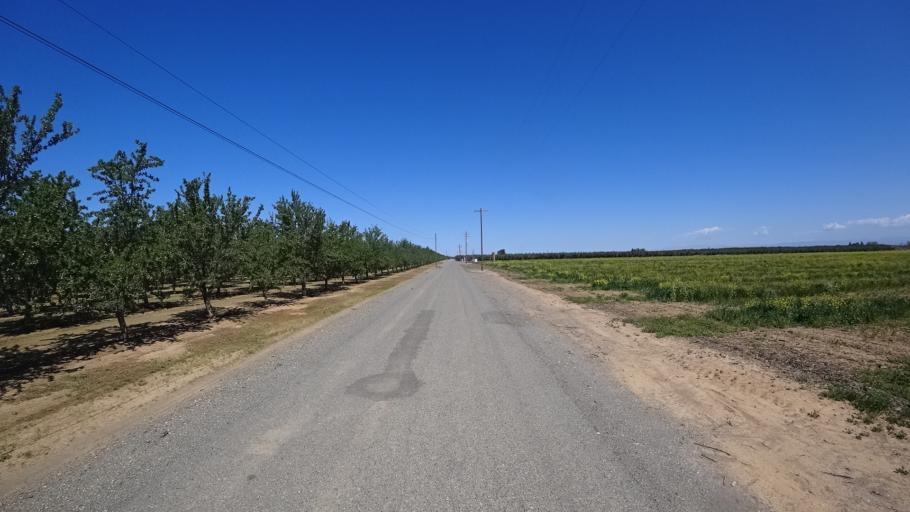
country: US
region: California
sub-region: Glenn County
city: Orland
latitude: 39.6991
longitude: -122.1639
